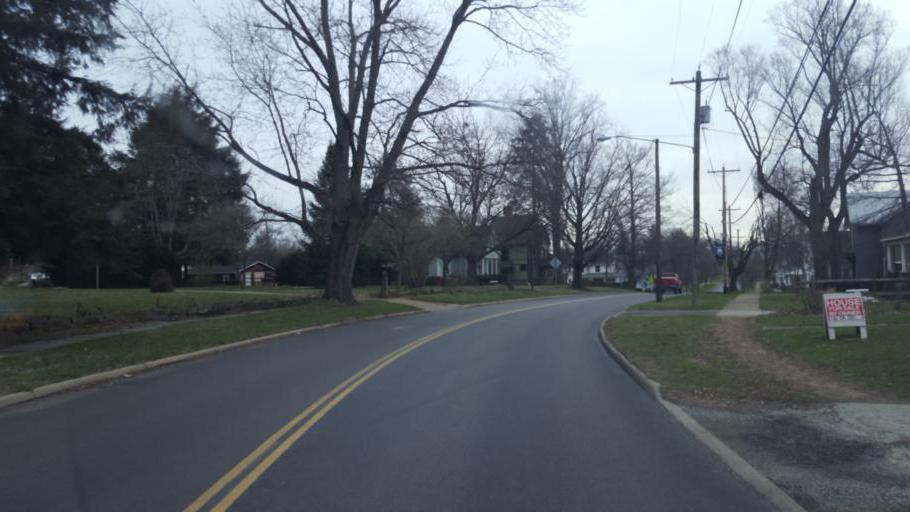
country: US
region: Ohio
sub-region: Knox County
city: Fredericktown
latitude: 40.4812
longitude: -82.5490
